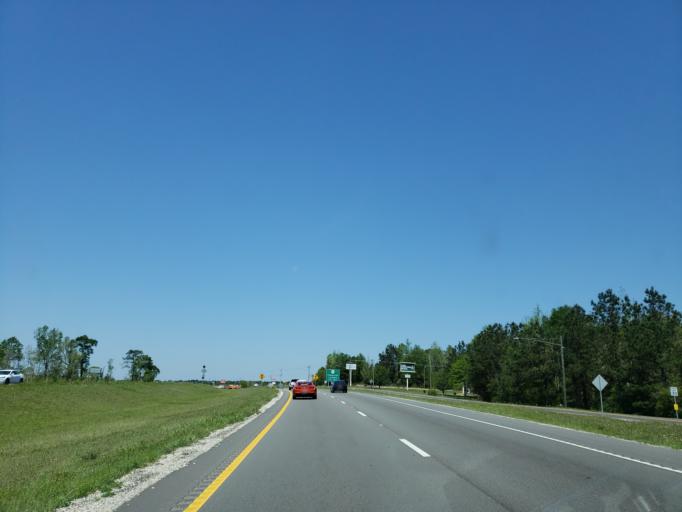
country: US
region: Mississippi
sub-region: Stone County
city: Wiggins
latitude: 30.8381
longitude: -89.1384
